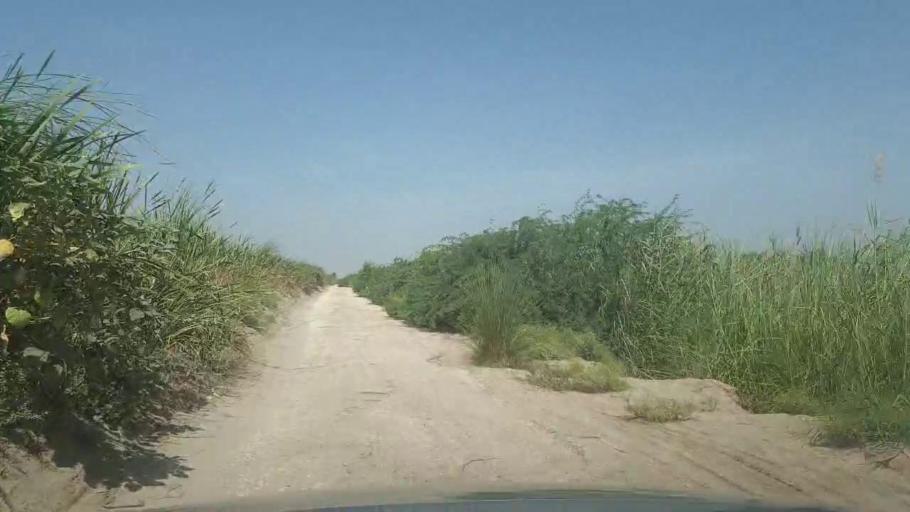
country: PK
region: Sindh
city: Khairpur
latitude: 27.3984
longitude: 69.0625
